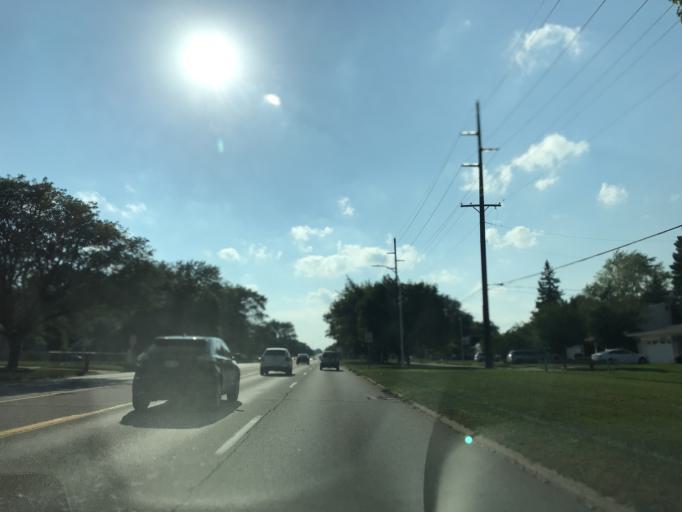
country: US
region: Michigan
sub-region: Wayne County
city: Plymouth
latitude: 42.3963
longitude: -83.4194
